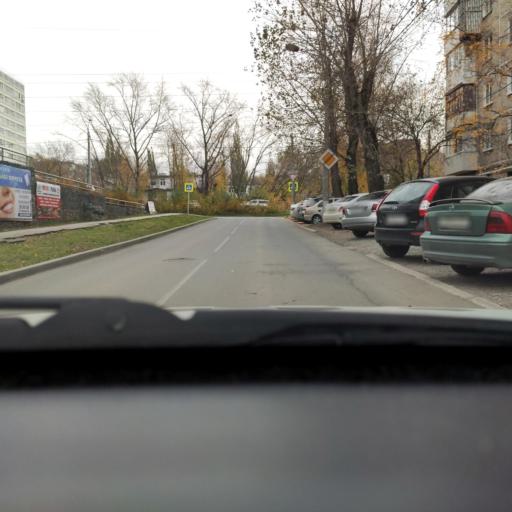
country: RU
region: Perm
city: Kondratovo
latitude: 57.9696
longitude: 56.1668
